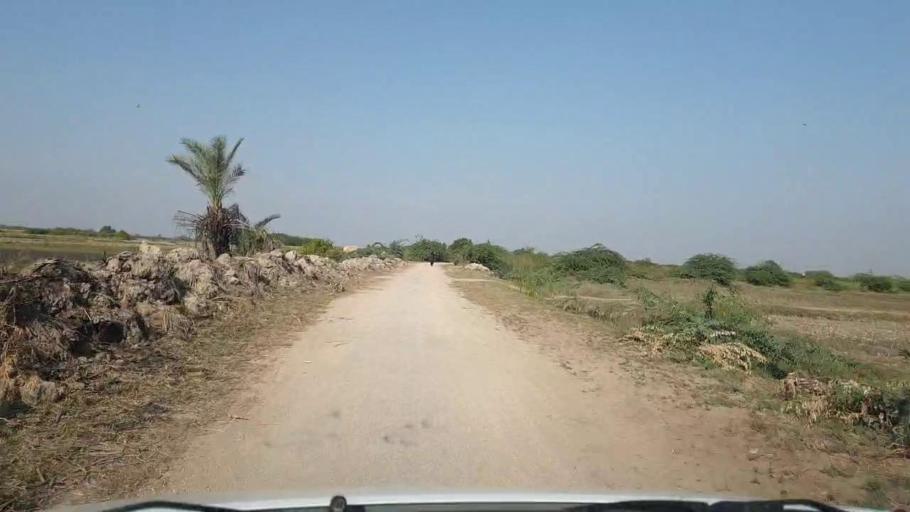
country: PK
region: Sindh
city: Mirpur Sakro
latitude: 24.5979
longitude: 67.6300
